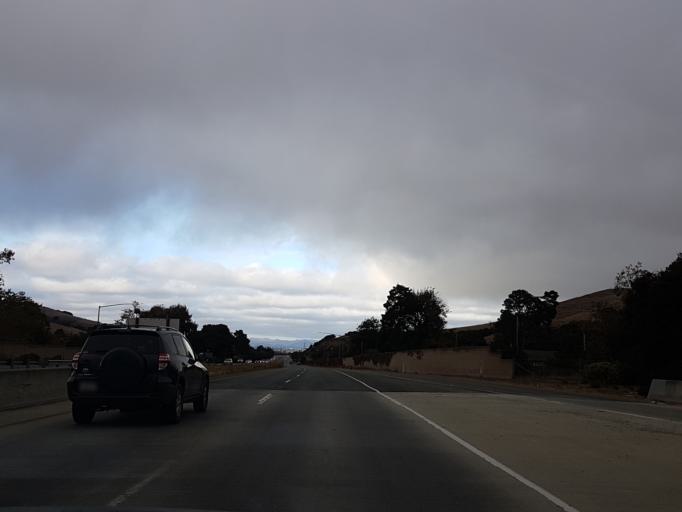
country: US
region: California
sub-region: Monterey County
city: Salinas
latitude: 36.6072
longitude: -121.6929
